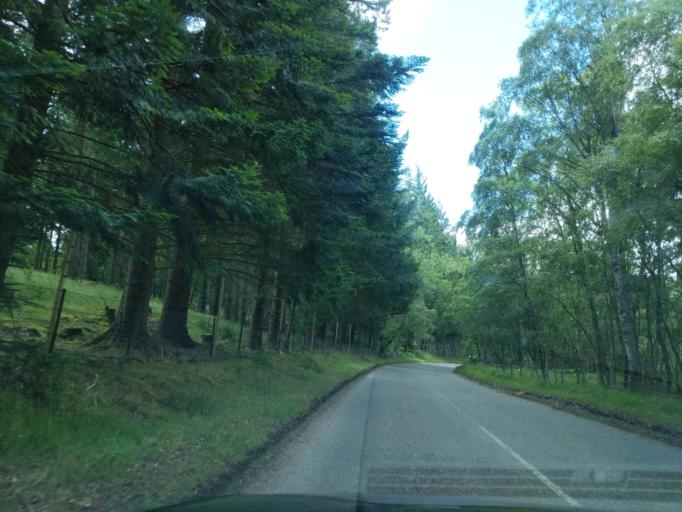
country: GB
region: Scotland
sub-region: Aberdeenshire
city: Ballater
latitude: 57.0659
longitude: -2.9121
